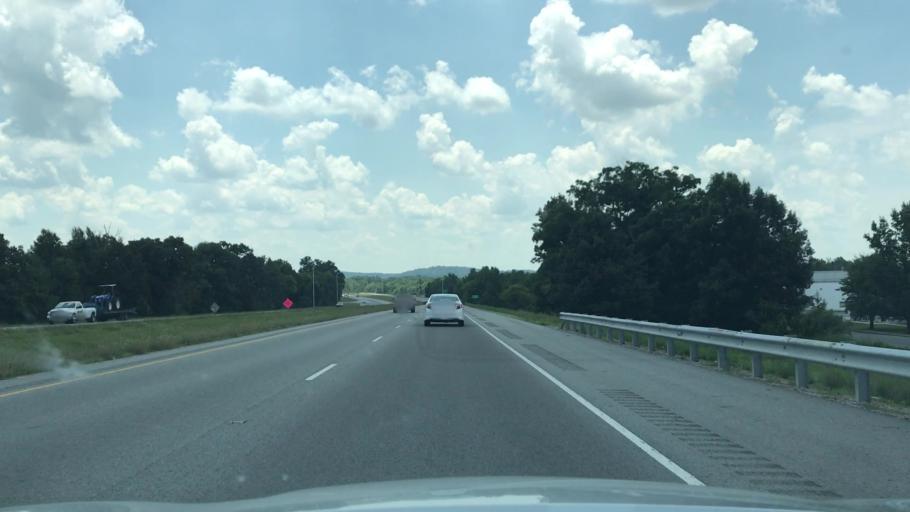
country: US
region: Tennessee
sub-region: Putnam County
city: Algood
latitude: 36.1880
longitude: -85.4622
